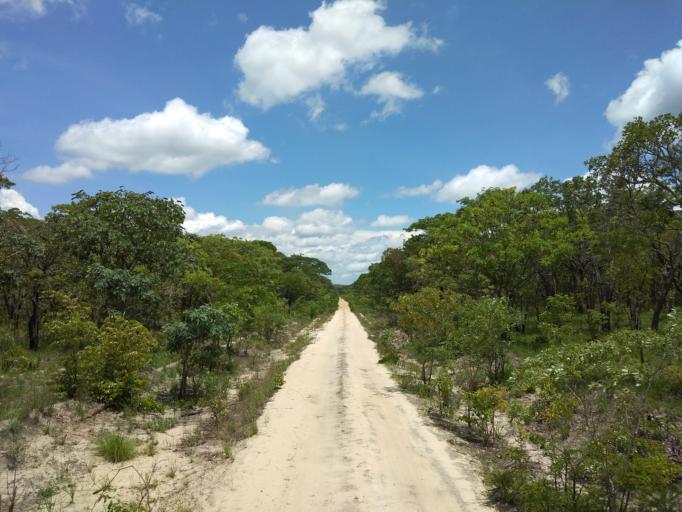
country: ZM
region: Central
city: Mkushi
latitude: -13.9580
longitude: 29.9014
